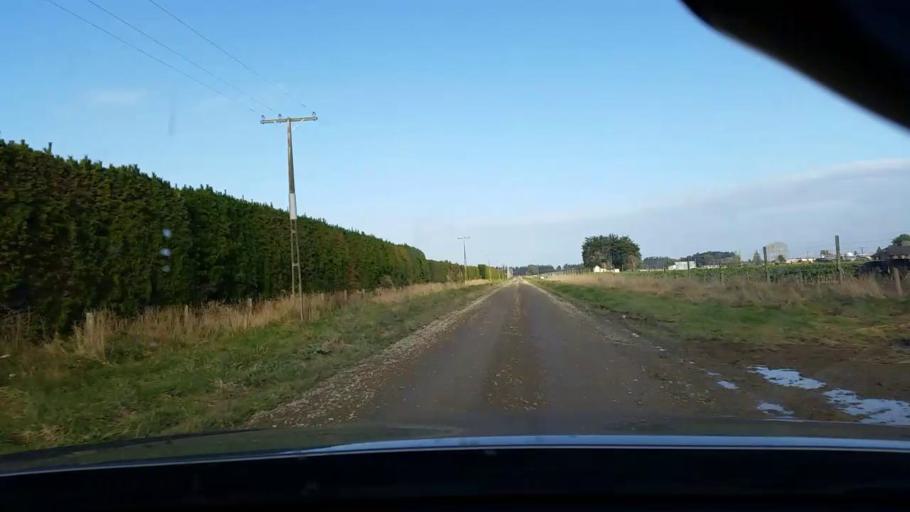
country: NZ
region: Southland
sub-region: Invercargill City
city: Invercargill
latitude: -46.2865
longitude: 168.2947
